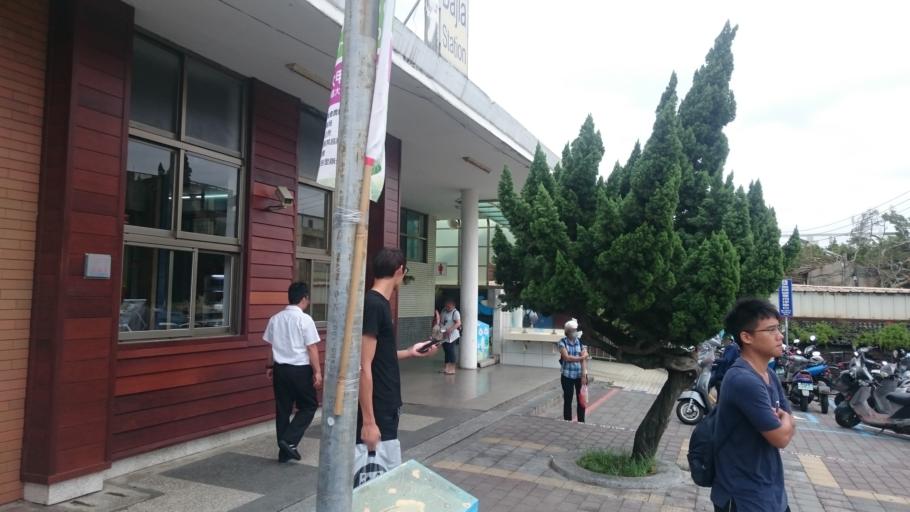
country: TW
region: Taiwan
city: Fengyuan
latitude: 24.3445
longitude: 120.6269
